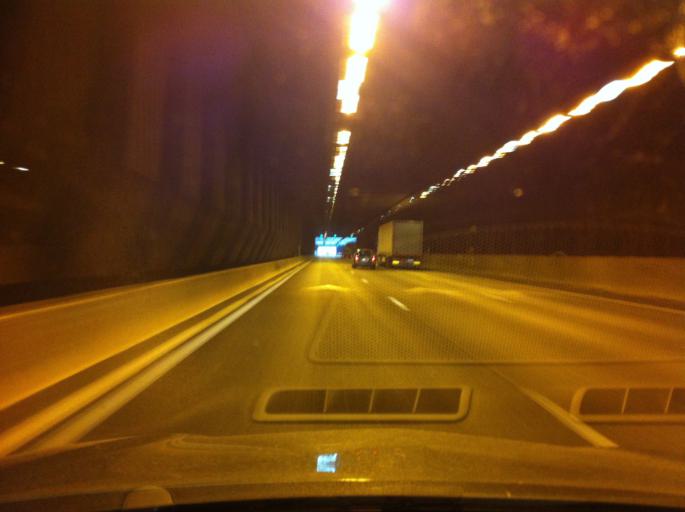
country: FR
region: Ile-de-France
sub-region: Departement du Val-d'Oise
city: Roissy-en-France
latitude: 49.0208
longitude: 2.5342
